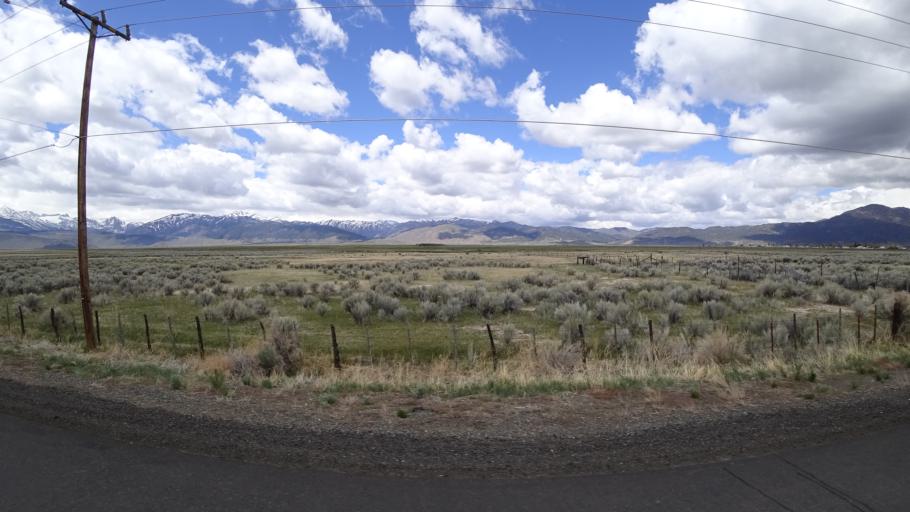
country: US
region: California
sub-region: Mono County
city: Bridgeport
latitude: 38.2426
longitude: -119.2217
